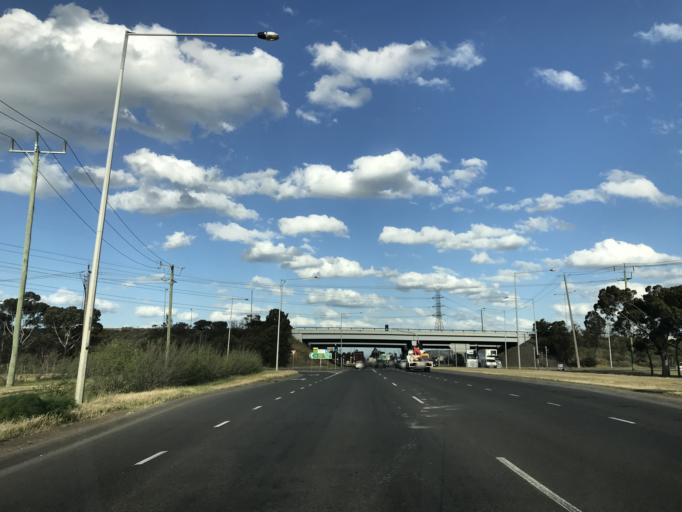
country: AU
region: Victoria
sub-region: Brimbank
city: Sunshine West
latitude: -37.8150
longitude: 144.8063
